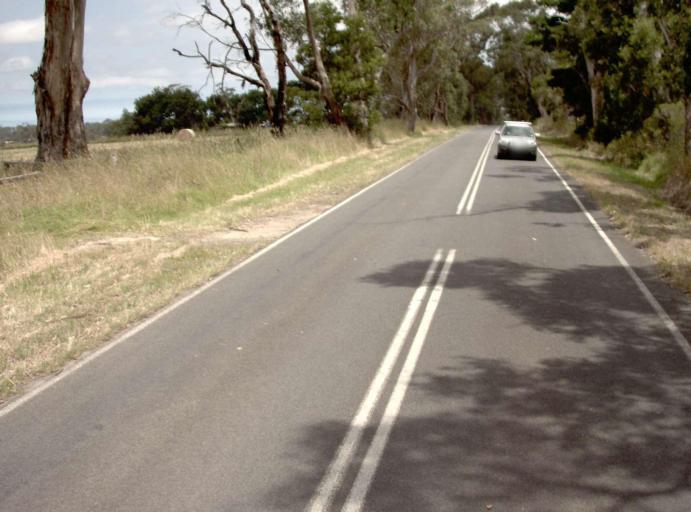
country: AU
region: Victoria
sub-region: Latrobe
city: Traralgon
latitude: -38.5087
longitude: 146.6497
